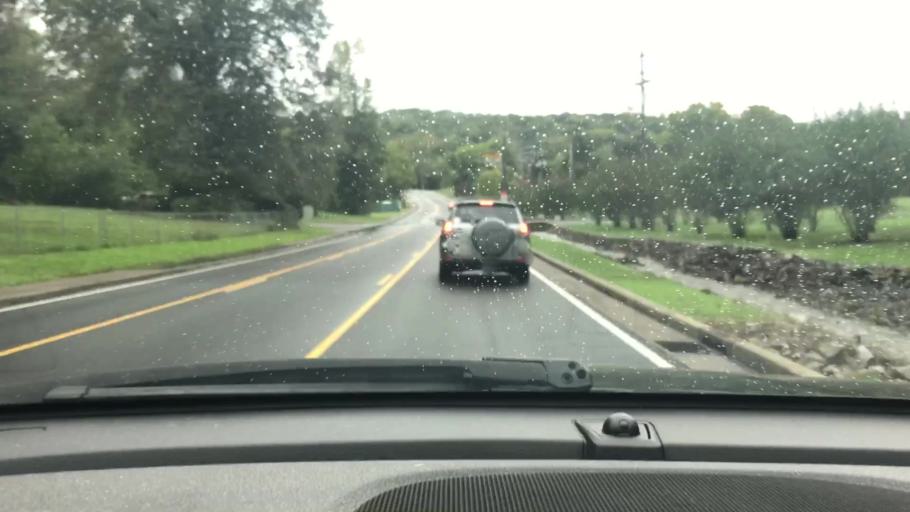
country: US
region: Tennessee
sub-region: Cheatham County
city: Kingston Springs
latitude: 36.0885
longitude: -87.1064
